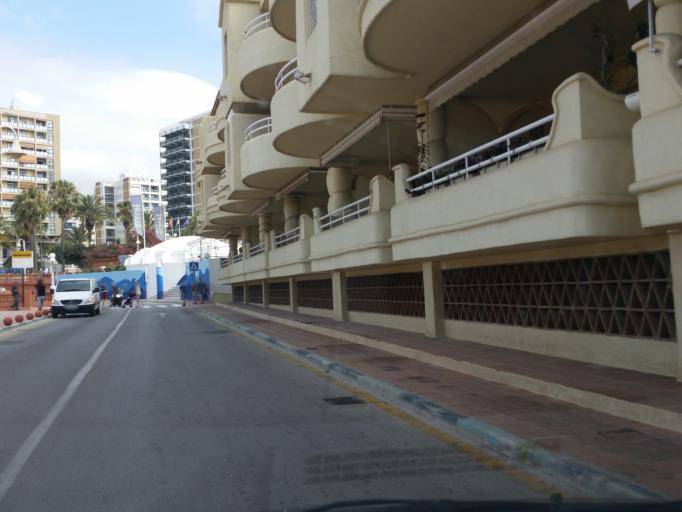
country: ES
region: Andalusia
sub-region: Provincia de Malaga
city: Torremolinos
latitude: 36.5960
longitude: -4.5151
